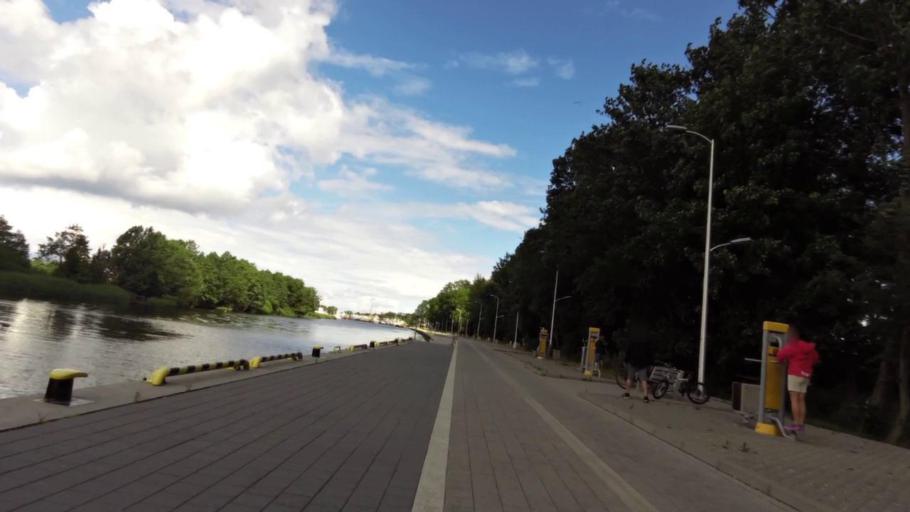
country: PL
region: West Pomeranian Voivodeship
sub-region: Powiat slawienski
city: Darlowo
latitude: 54.4311
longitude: 16.3923
